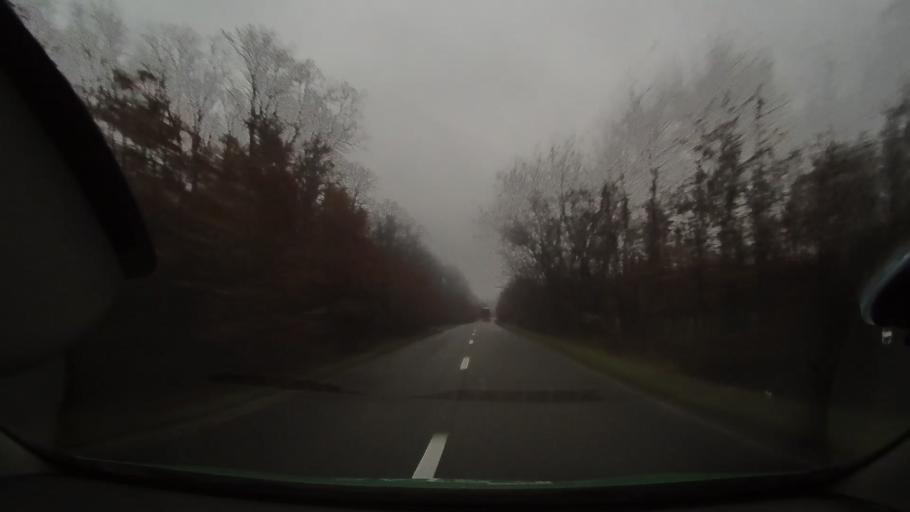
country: RO
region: Arad
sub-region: Comuna Beliu
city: Beliu
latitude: 46.5151
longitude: 21.9579
